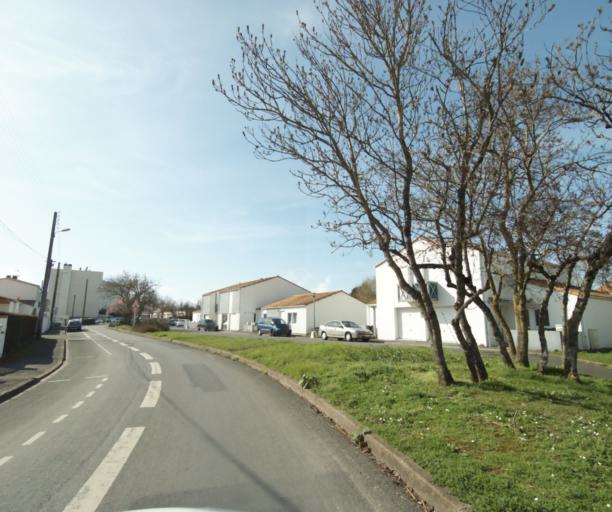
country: FR
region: Poitou-Charentes
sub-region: Departement de la Charente-Maritime
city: La Rochelle
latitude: 46.1712
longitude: -1.1723
